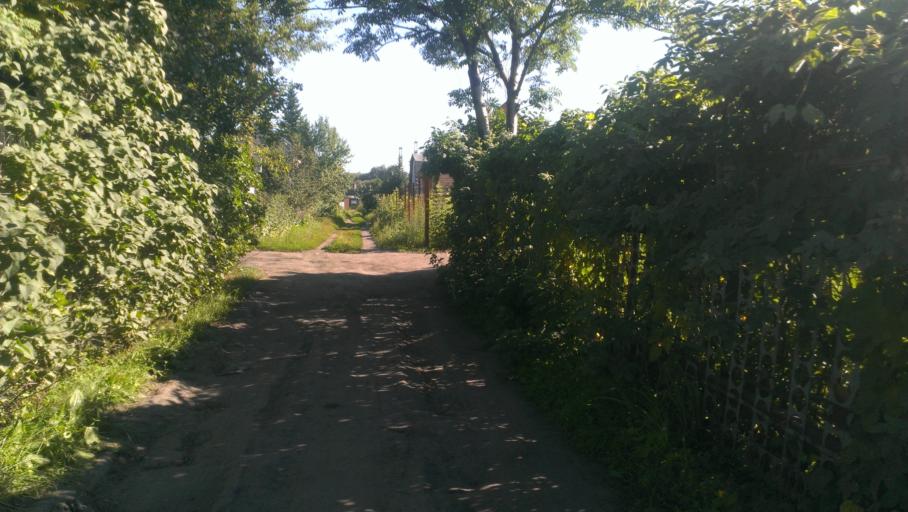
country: RU
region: Altai Krai
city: Novosilikatnyy
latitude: 53.3223
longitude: 83.6695
